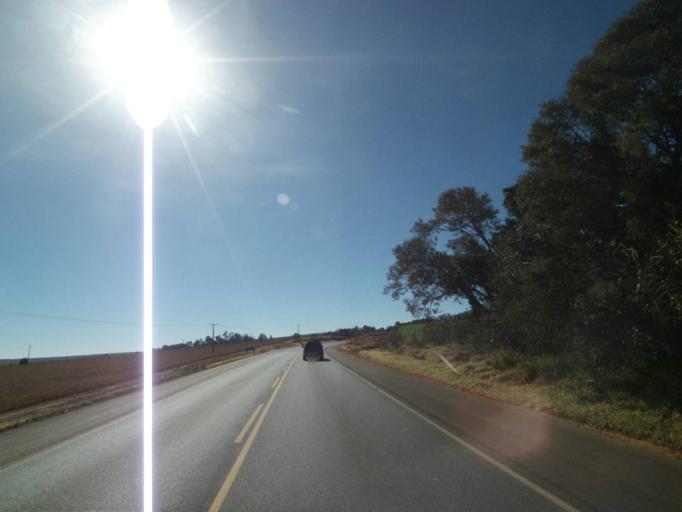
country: BR
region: Parana
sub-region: Tibagi
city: Tibagi
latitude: -24.3720
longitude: -50.3265
